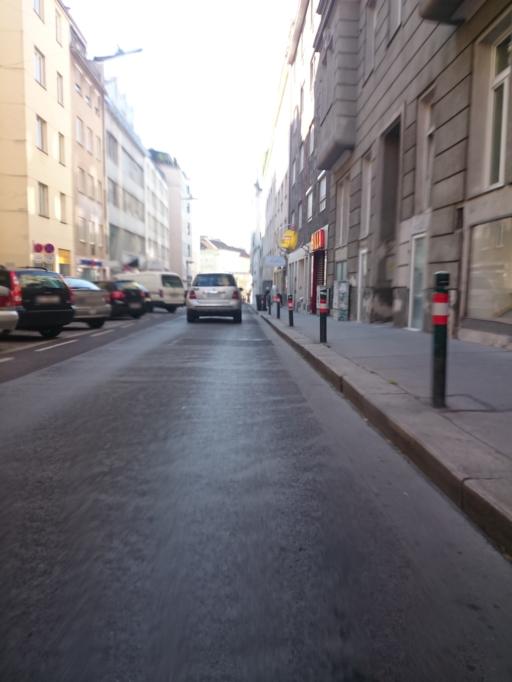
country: AT
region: Vienna
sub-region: Wien Stadt
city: Vienna
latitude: 48.2076
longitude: 16.3491
